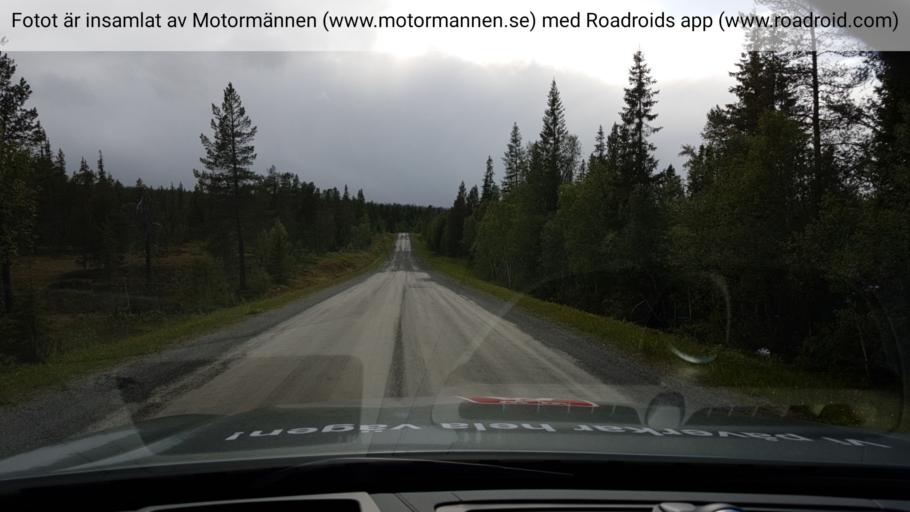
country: NO
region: Nord-Trondelag
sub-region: Snasa
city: Snaase
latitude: 63.7128
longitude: 12.4429
